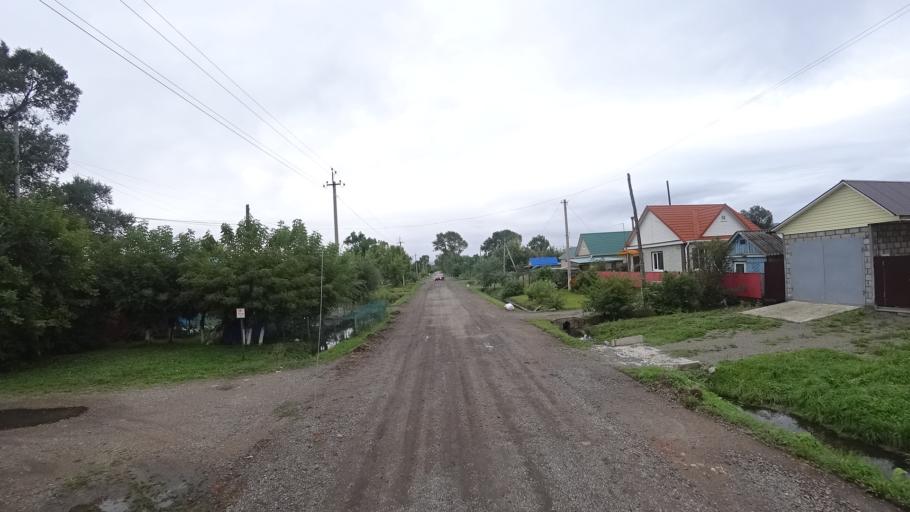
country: RU
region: Primorskiy
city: Chernigovka
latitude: 44.3452
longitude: 132.5814
